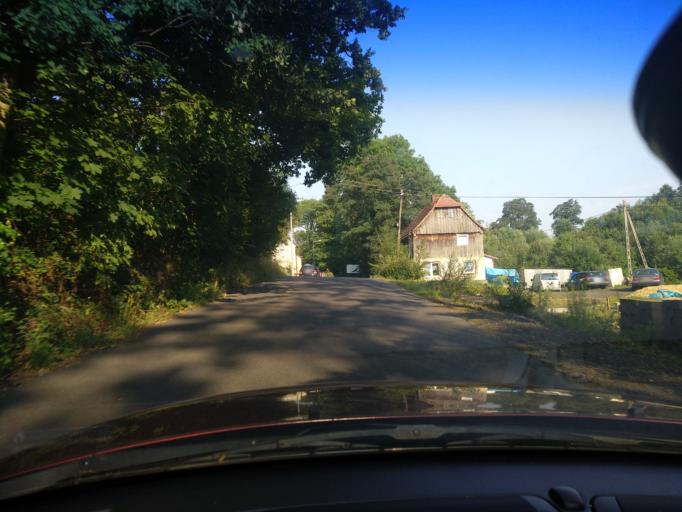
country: PL
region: Lower Silesian Voivodeship
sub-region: Powiat lubanski
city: Siekierczyn
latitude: 51.0605
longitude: 15.1738
